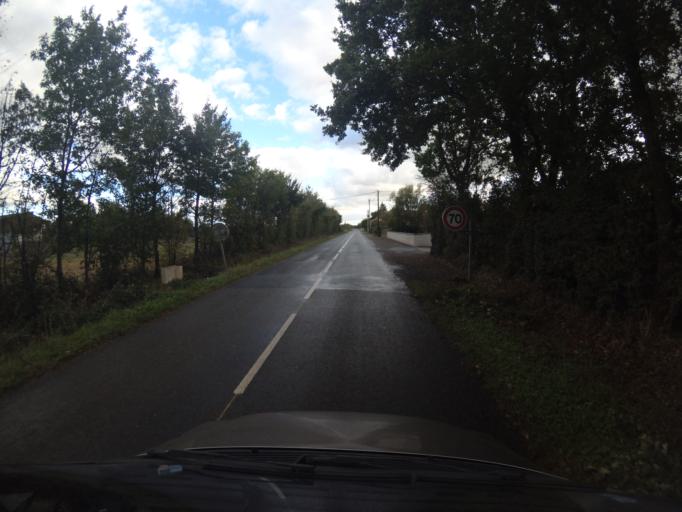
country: FR
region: Pays de la Loire
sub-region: Departement de la Loire-Atlantique
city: Saint-Lumine-de-Clisson
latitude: 47.0722
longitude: -1.3254
